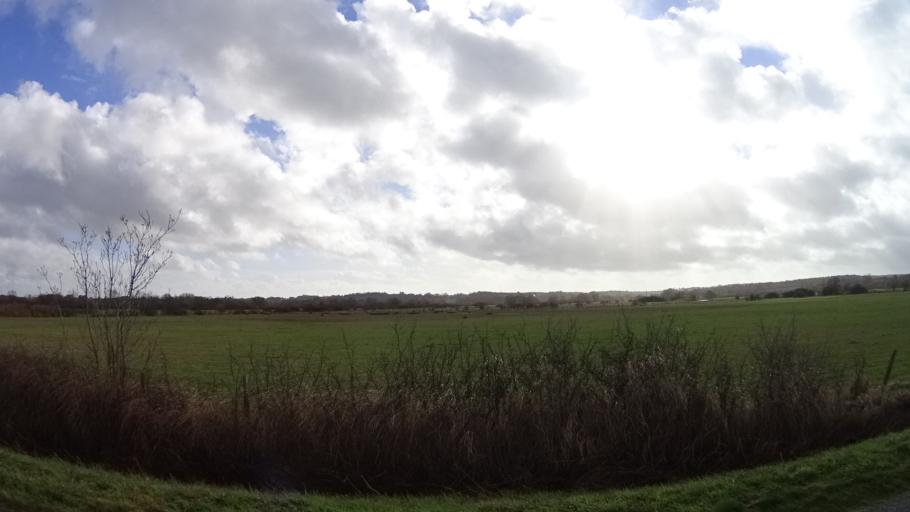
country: FR
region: Brittany
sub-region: Departement du Morbihan
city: Rieux
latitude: 47.5785
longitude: -2.0972
